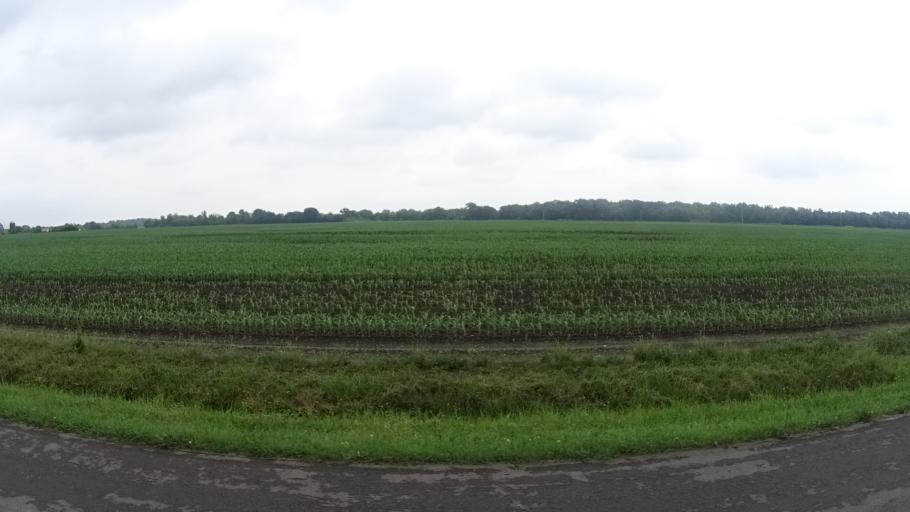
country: US
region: Ohio
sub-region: Huron County
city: Bellevue
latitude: 41.3577
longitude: -82.7857
